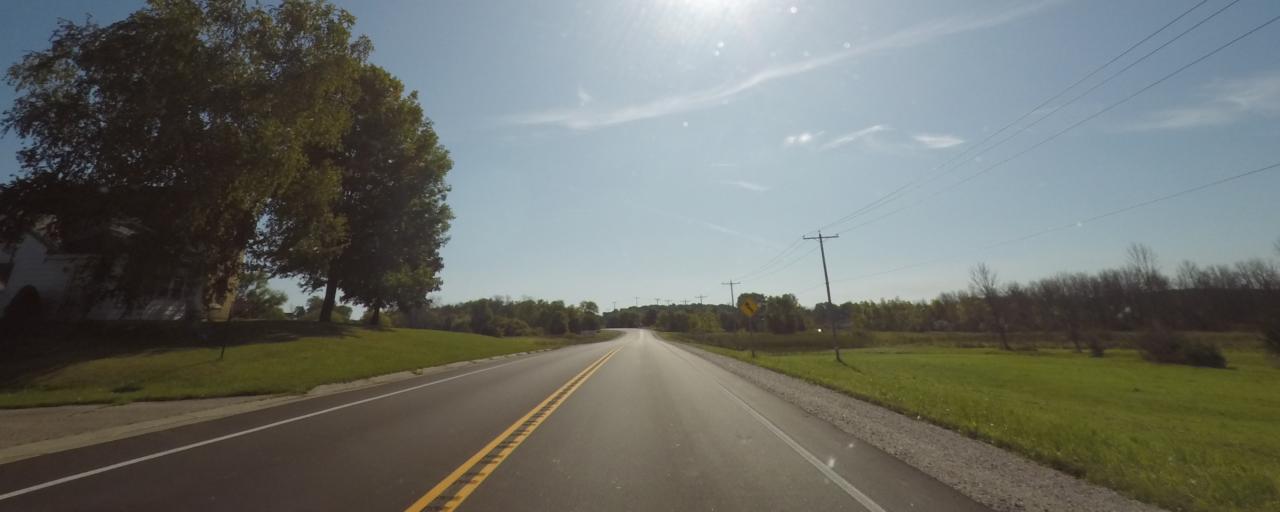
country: US
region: Wisconsin
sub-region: Jefferson County
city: Johnson Creek
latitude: 43.0140
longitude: -88.6739
